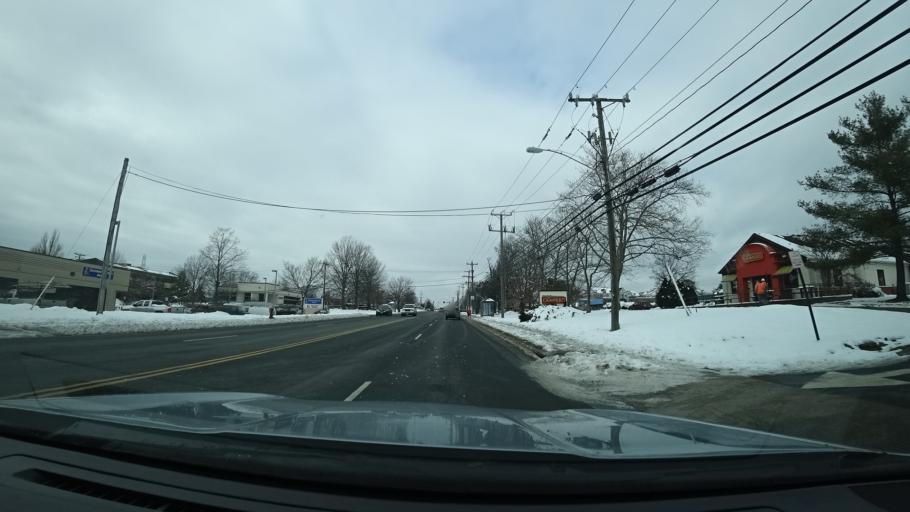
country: US
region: Virginia
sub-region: Fairfax County
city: Herndon
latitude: 38.9684
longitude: -77.3777
